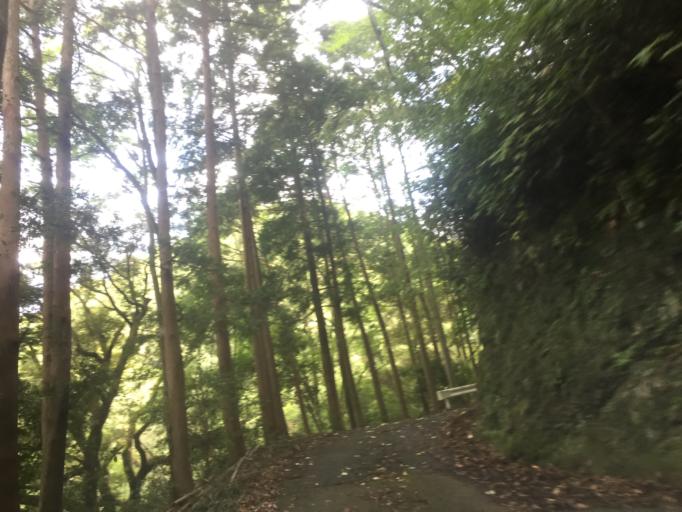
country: JP
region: Shizuoka
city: Kanaya
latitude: 34.8425
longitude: 138.0584
